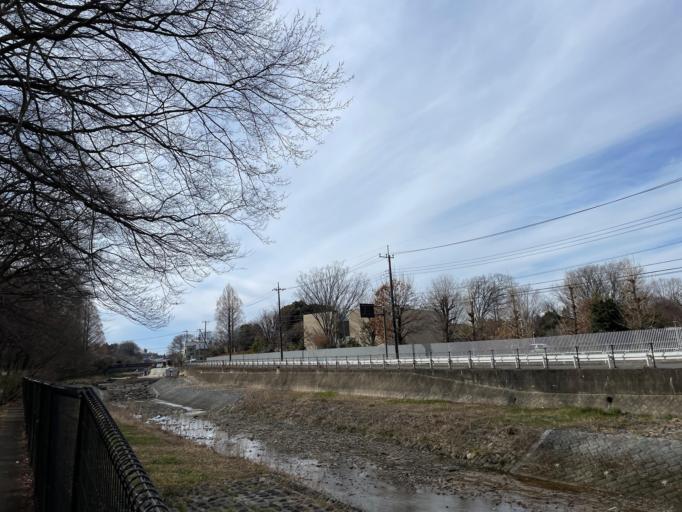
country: JP
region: Saitama
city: Tokorozawa
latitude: 35.7812
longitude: 139.5076
